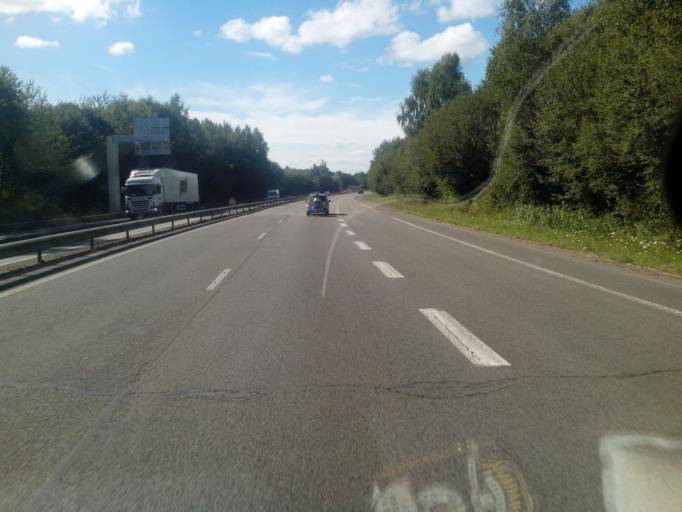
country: FR
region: Pays de la Loire
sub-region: Departement de la Loire-Atlantique
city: Orvault
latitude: 47.2791
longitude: -1.6007
